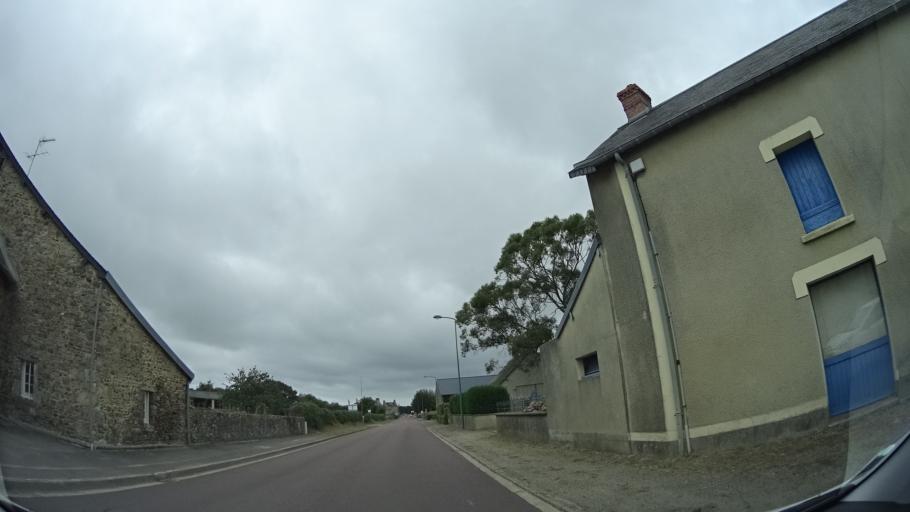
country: FR
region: Lower Normandy
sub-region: Departement de la Manche
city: La Haye-du-Puits
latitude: 49.3004
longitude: -1.5726
